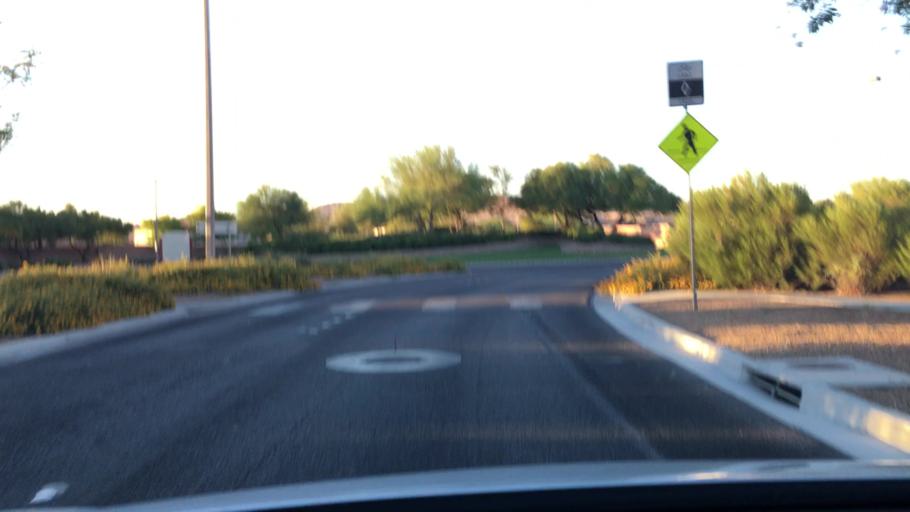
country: US
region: Nevada
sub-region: Clark County
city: Summerlin South
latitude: 36.1202
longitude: -115.3350
